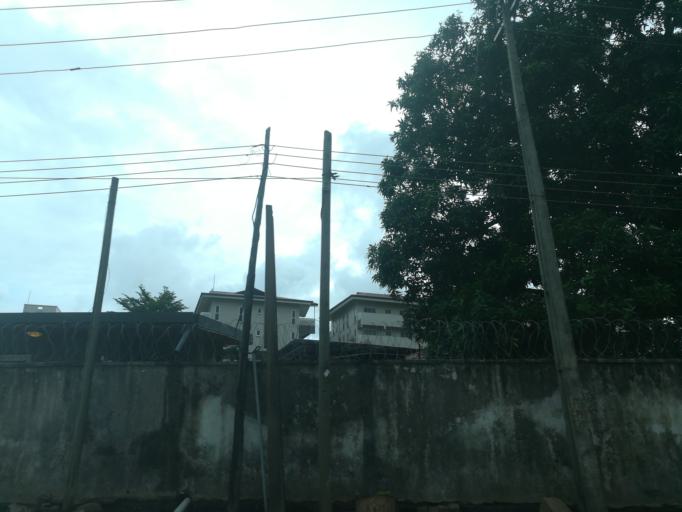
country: NG
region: Lagos
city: Lagos
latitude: 6.4359
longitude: 3.4128
